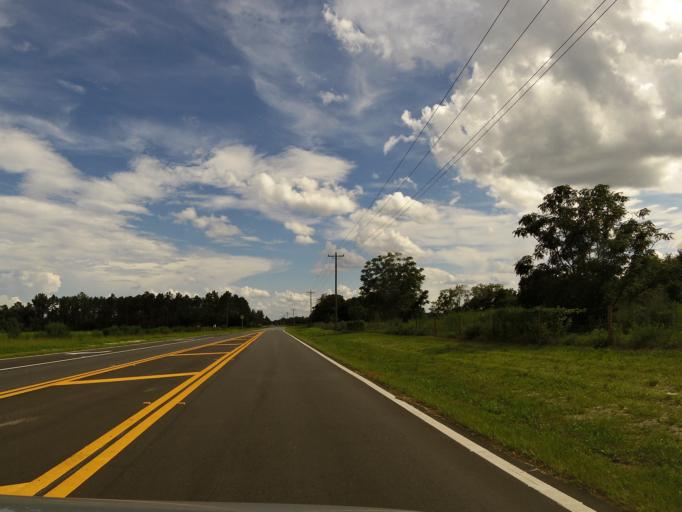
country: US
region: Florida
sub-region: Clay County
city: Green Cove Springs
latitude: 30.0147
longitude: -81.7316
